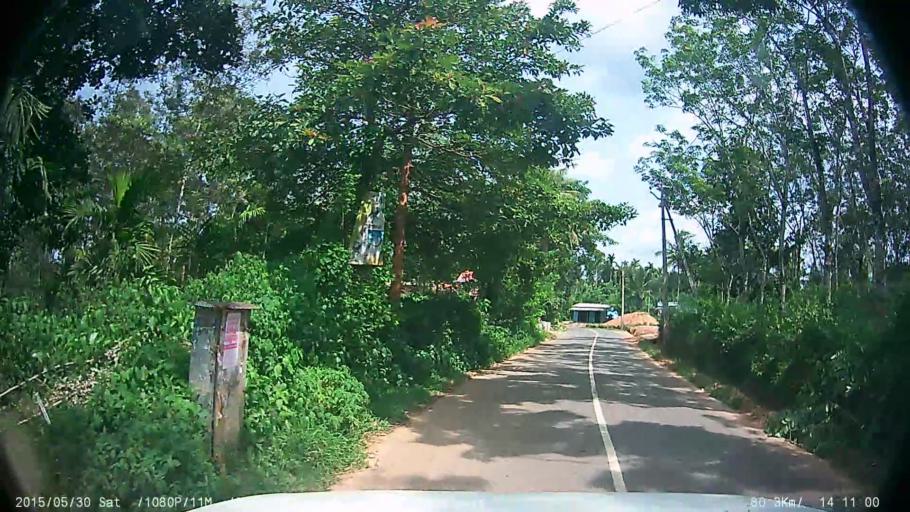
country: IN
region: Kerala
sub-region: Wayanad
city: Panamaram
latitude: 11.7950
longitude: 76.0528
